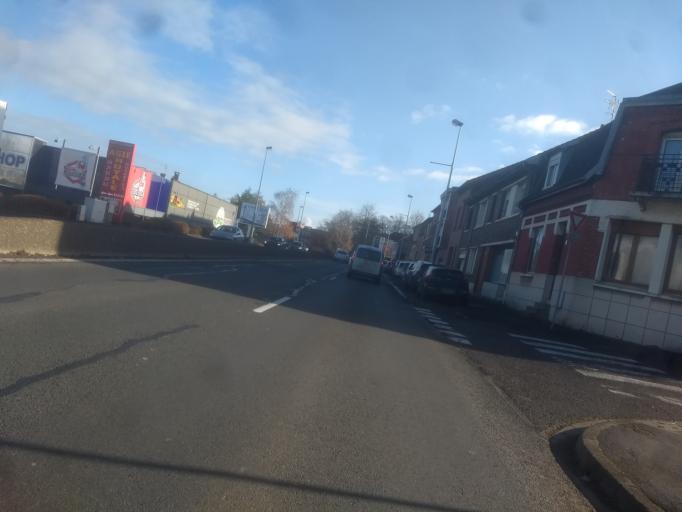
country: FR
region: Nord-Pas-de-Calais
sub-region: Departement du Pas-de-Calais
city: Sainte-Catherine
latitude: 50.2974
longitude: 2.7523
